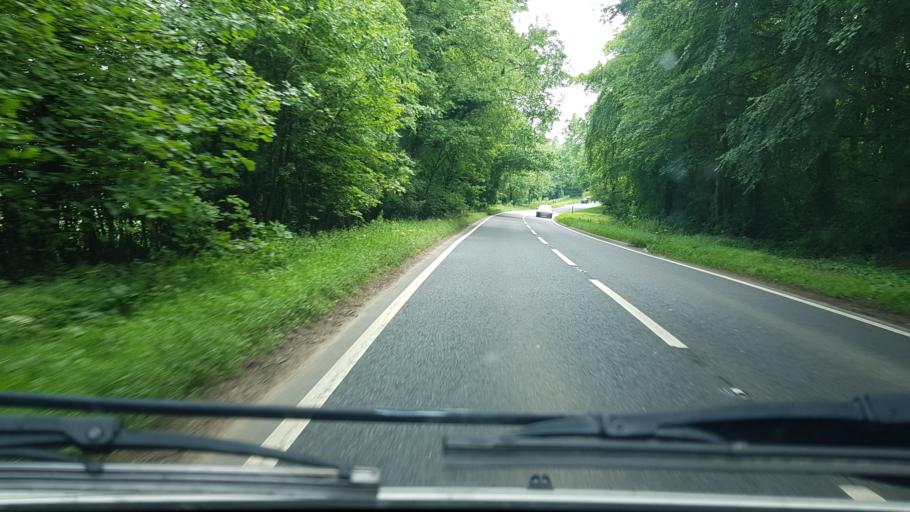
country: GB
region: England
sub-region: Worcestershire
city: Broadway
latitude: 52.0284
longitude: -1.8239
